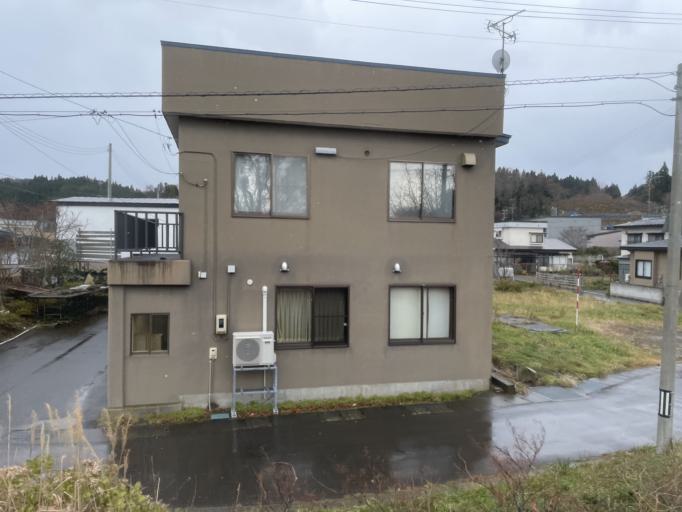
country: JP
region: Aomori
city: Goshogawara
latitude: 41.1791
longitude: 140.4912
